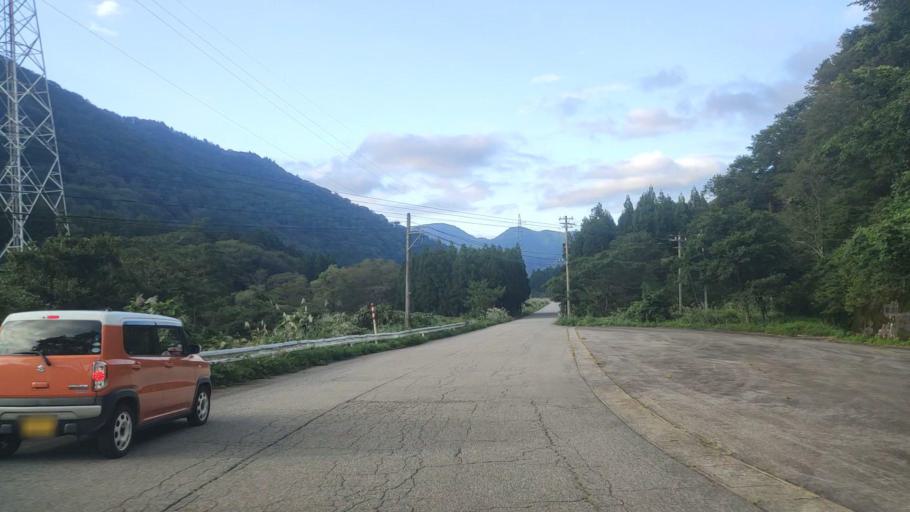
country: JP
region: Toyama
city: Yatsuomachi-higashikumisaka
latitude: 36.4531
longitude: 137.0844
